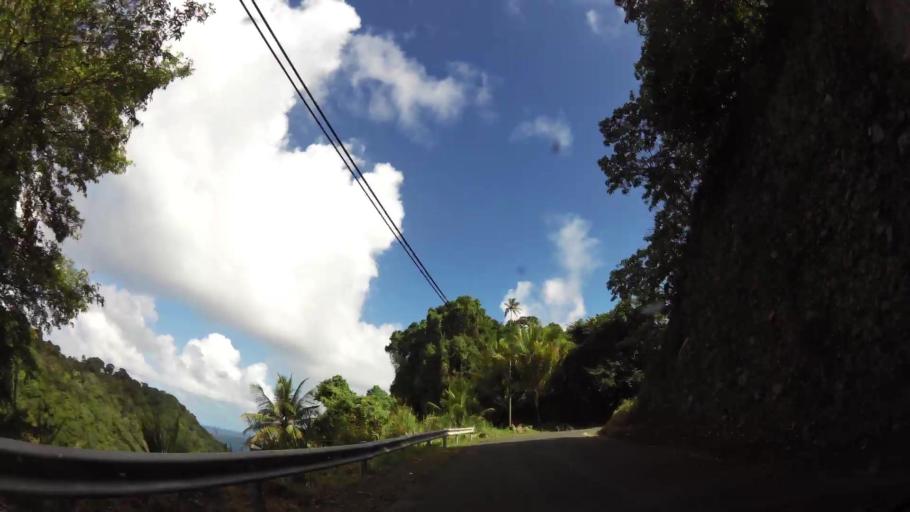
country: DM
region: Saint John
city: Portsmouth
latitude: 15.6198
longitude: -61.4167
